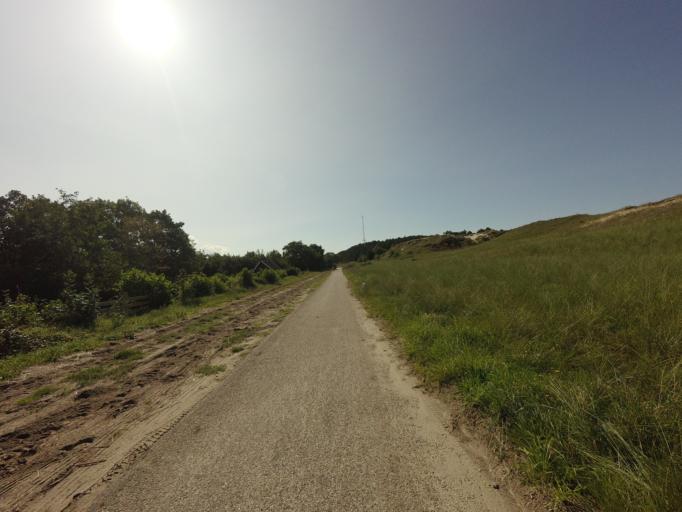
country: NL
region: Friesland
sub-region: Gemeente Terschelling
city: West-Terschelling
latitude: 53.4020
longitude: 5.3532
